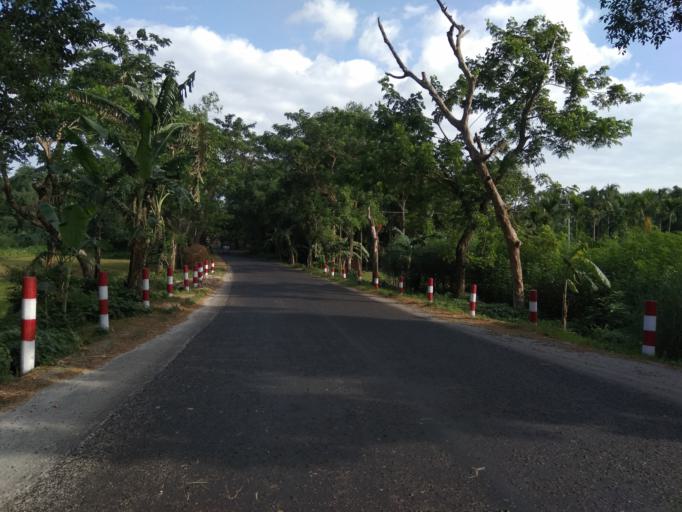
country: BD
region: Rangpur Division
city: Rangpur
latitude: 25.8393
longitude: 89.1138
